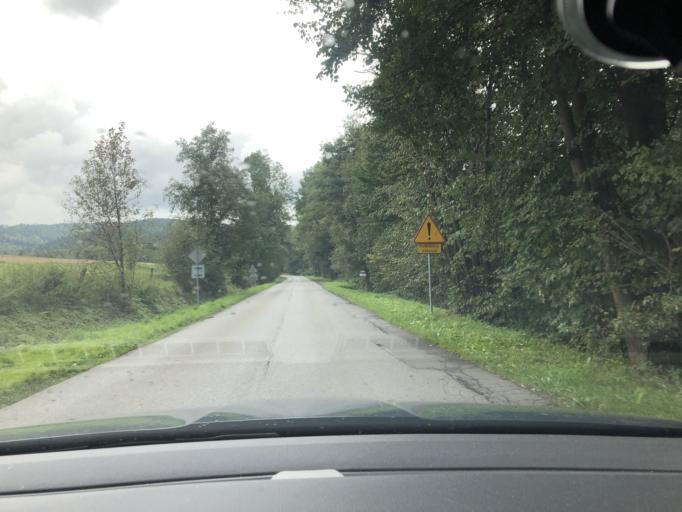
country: PL
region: Silesian Voivodeship
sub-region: Powiat zywiecki
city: Slemien
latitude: 49.7237
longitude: 19.3770
